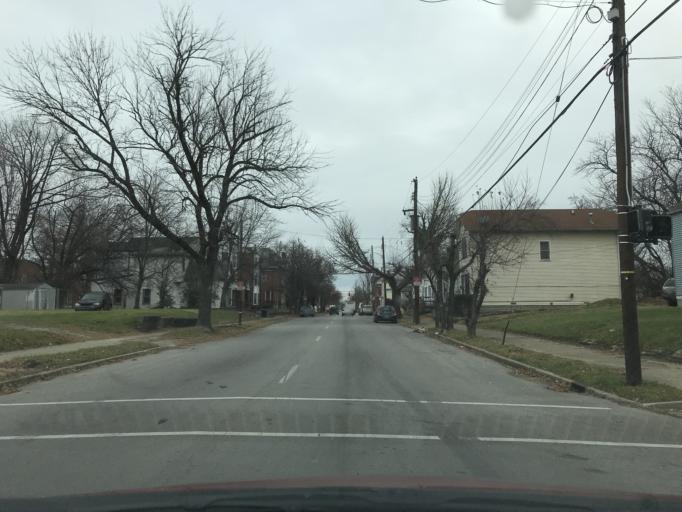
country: US
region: Kentucky
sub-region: Jefferson County
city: Louisville
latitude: 38.2508
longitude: -85.7862
